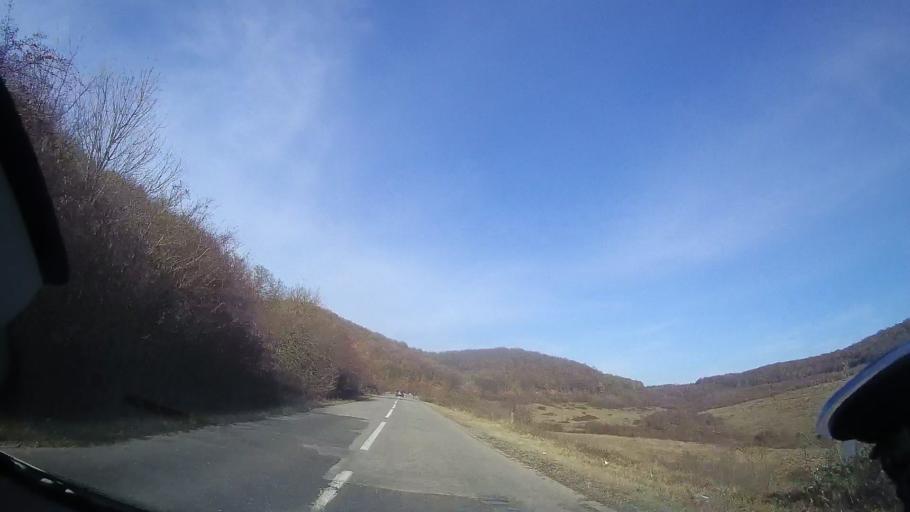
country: RO
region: Bihor
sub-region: Comuna Tileagd
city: Tileagd
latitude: 47.0918
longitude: 22.2358
